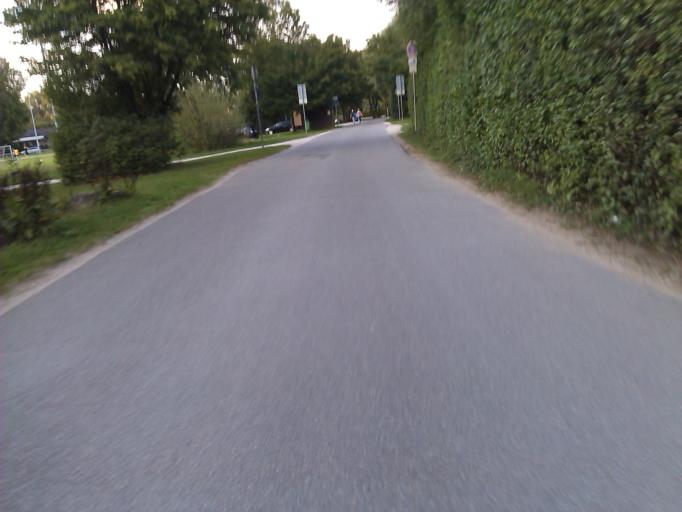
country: DE
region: Baden-Wuerttemberg
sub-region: Regierungsbezirk Stuttgart
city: Neckartailfingen
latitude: 48.6064
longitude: 9.2645
